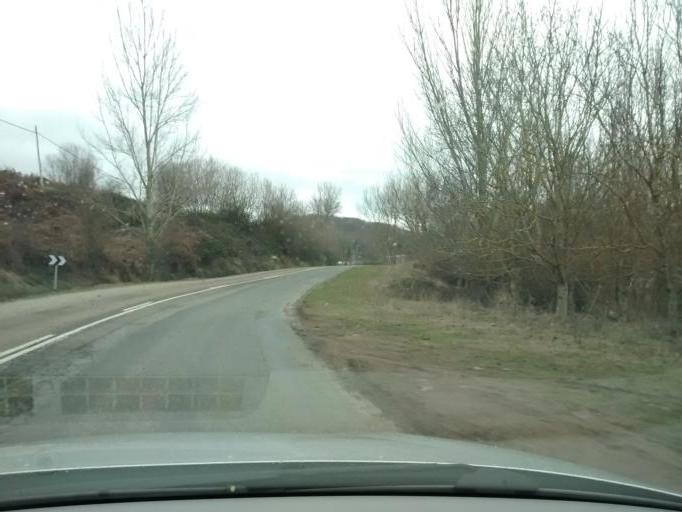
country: ES
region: Castille and Leon
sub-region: Provincia de Burgos
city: Espinosa de los Monteros
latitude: 43.0895
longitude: -3.5576
